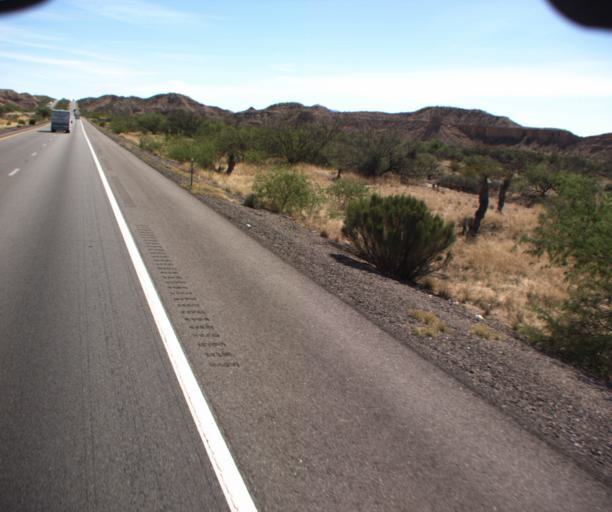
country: US
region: Arizona
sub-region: Cochise County
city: Benson
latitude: 31.9787
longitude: -110.2230
